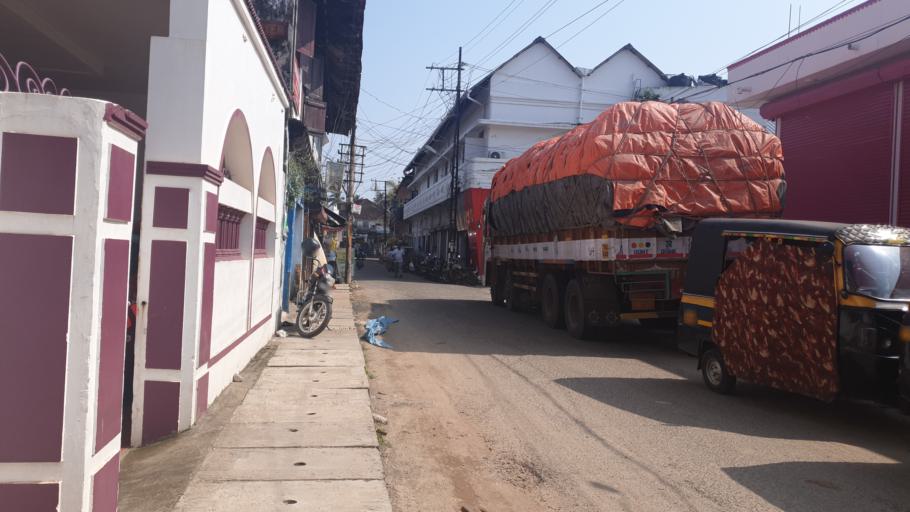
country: IN
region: Kerala
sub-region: Ernakulam
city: Cochin
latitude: 9.9634
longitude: 76.2568
